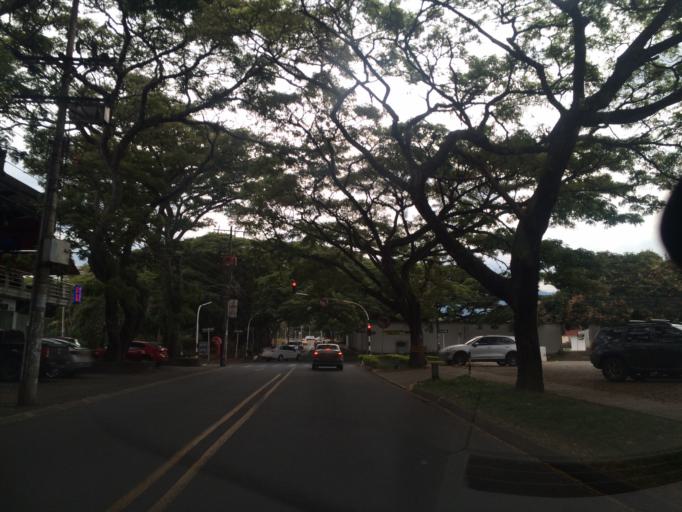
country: CO
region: Valle del Cauca
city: Cali
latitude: 3.3645
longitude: -76.5353
